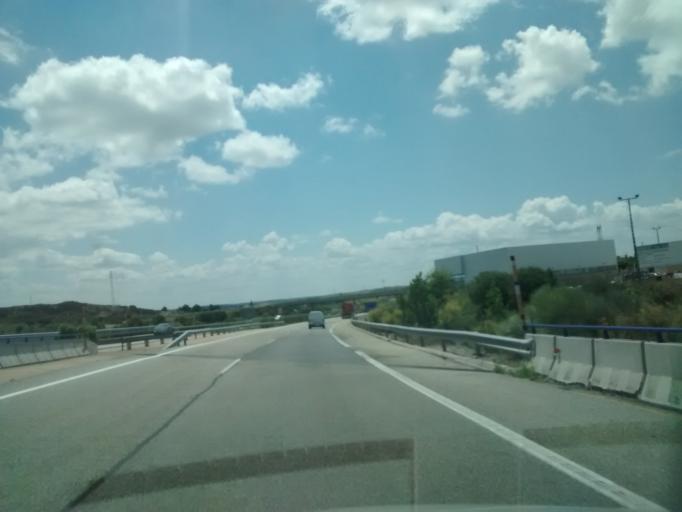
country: ES
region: Castille and Leon
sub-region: Provincia de Leon
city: Astorga
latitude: 42.4700
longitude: -6.0830
